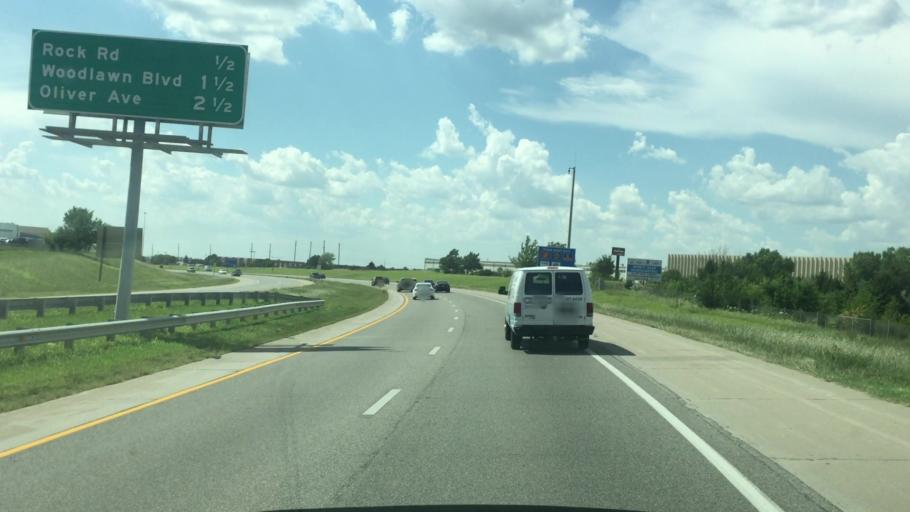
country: US
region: Kansas
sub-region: Sedgwick County
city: Bellaire
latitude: 37.7436
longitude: -97.2337
